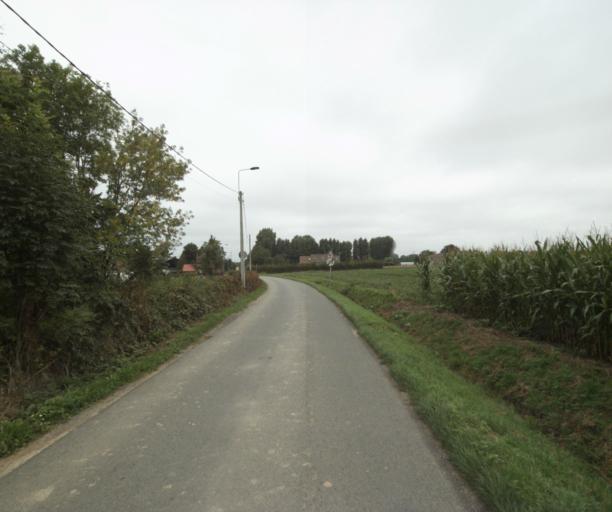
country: FR
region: Nord-Pas-de-Calais
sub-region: Departement du Nord
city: Sailly-lez-Lannoy
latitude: 50.6309
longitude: 3.2185
